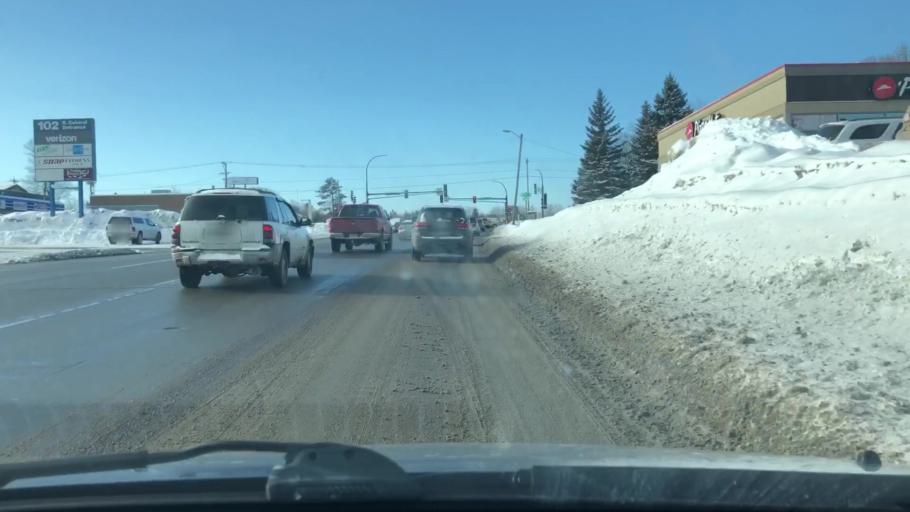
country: US
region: Minnesota
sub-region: Saint Louis County
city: Duluth
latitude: 46.8005
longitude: -92.1302
